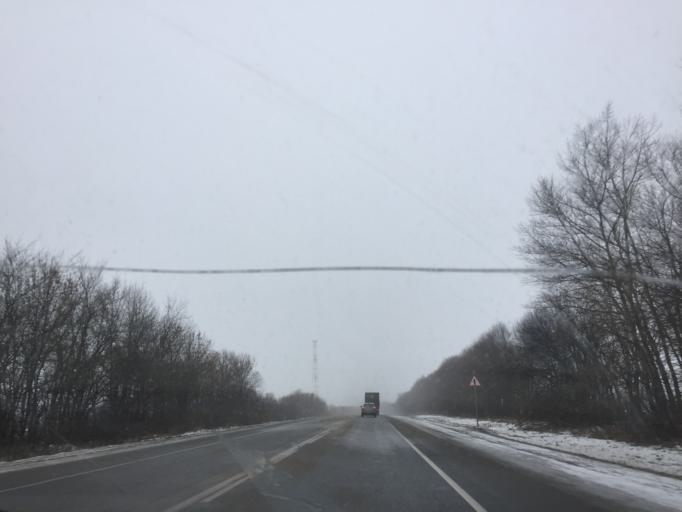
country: RU
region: Tula
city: Plavsk
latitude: 53.7883
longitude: 37.3669
